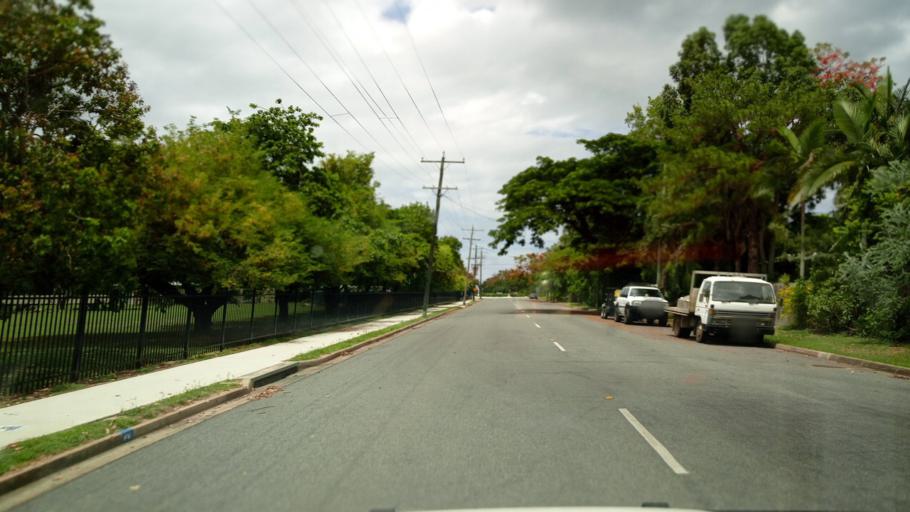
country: AU
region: Queensland
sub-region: Cairns
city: Redlynch
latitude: -16.8540
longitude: 145.7456
